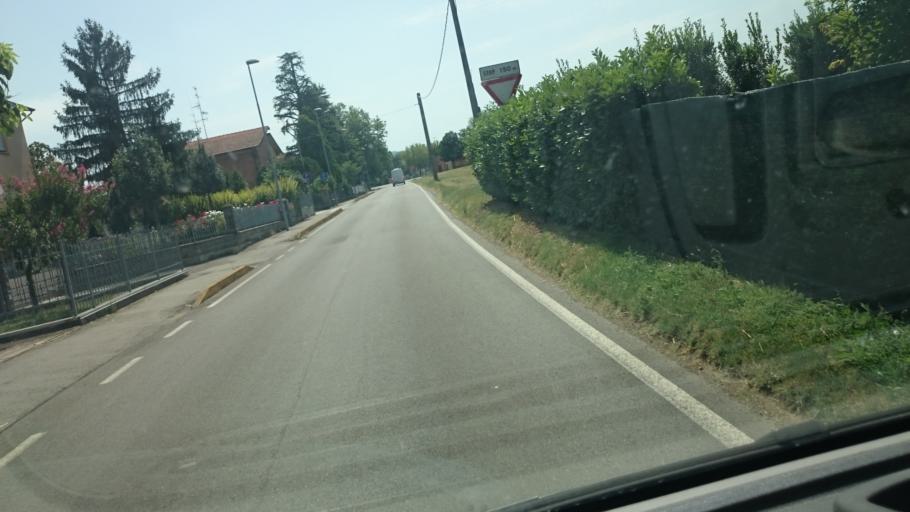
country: IT
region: Emilia-Romagna
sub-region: Provincia di Reggio Emilia
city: Fogliano
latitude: 44.6322
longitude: 10.6646
